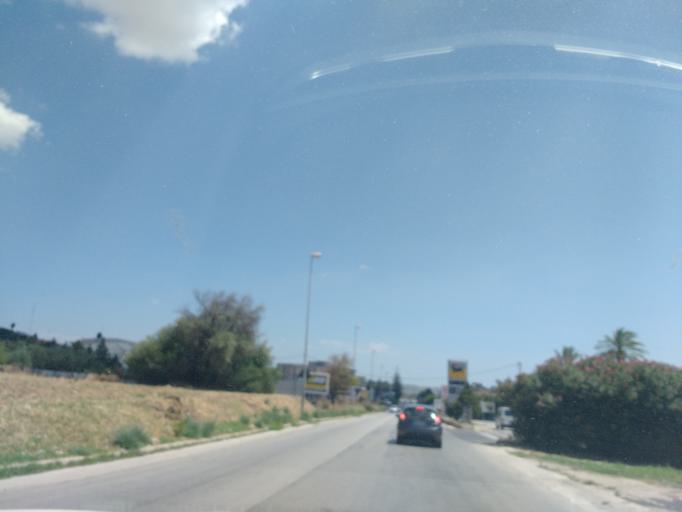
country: IT
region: Sicily
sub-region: Provincia di Siracusa
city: Rosolini
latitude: 36.8233
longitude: 14.9609
